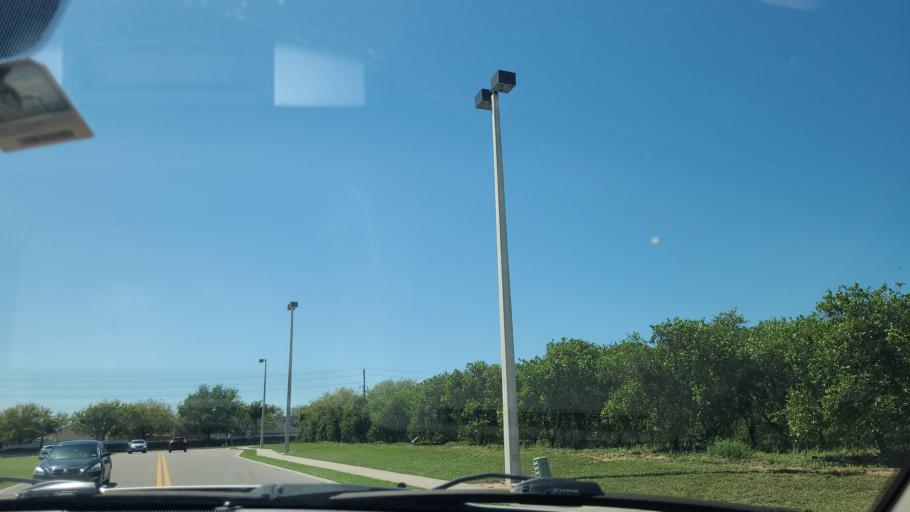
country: US
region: Florida
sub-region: Lake County
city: Tavares
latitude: 28.7835
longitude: -81.7505
